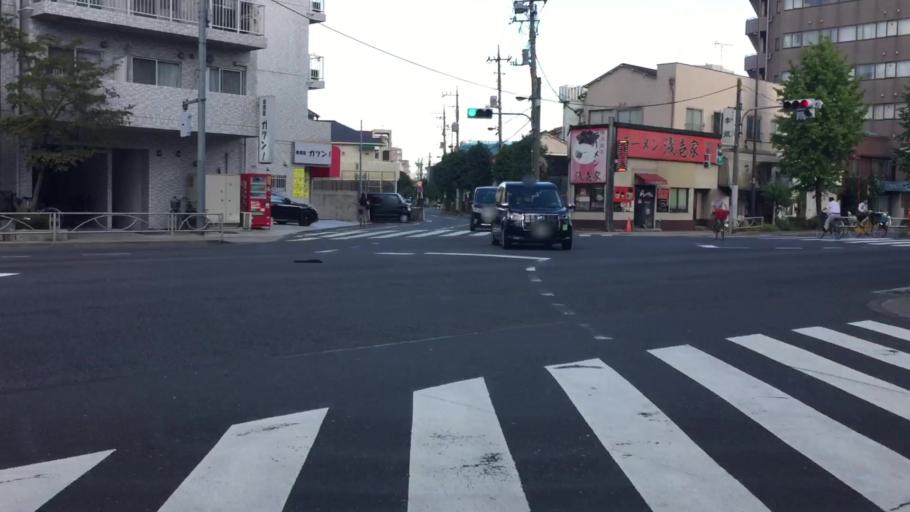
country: JP
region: Saitama
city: Soka
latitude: 35.7689
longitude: 139.8034
